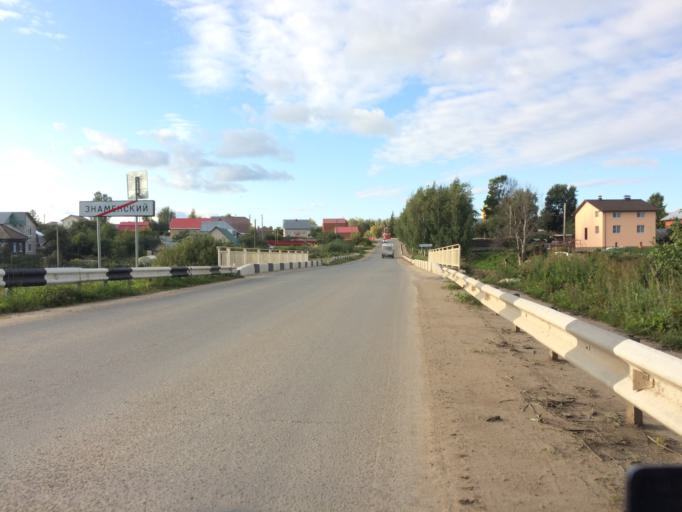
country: RU
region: Mariy-El
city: Yoshkar-Ola
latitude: 56.6480
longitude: 47.9810
